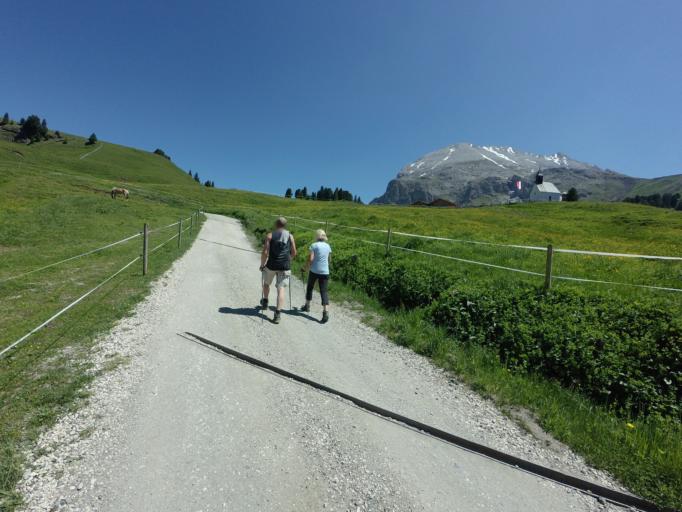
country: IT
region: Trentino-Alto Adige
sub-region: Provincia di Trento
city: Mazzin
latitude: 46.5112
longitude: 11.6858
